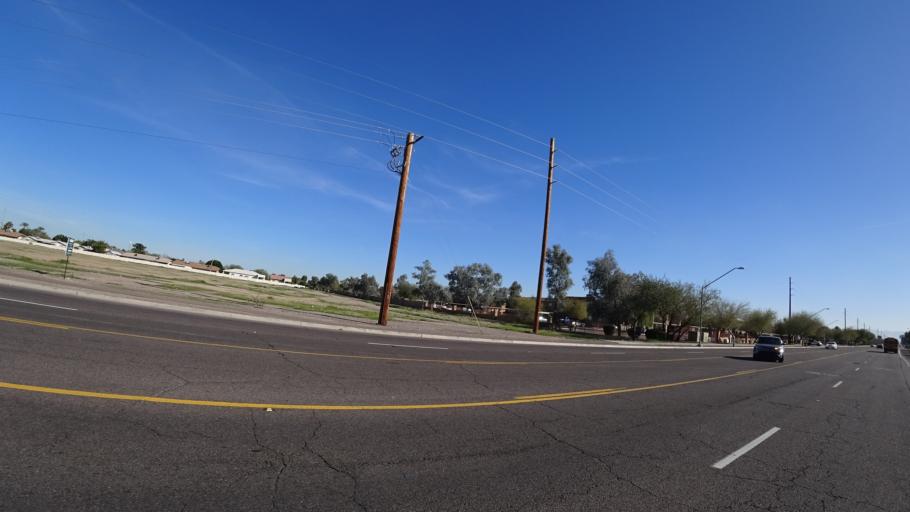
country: US
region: Arizona
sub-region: Maricopa County
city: Peoria
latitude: 33.5363
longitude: -112.2378
